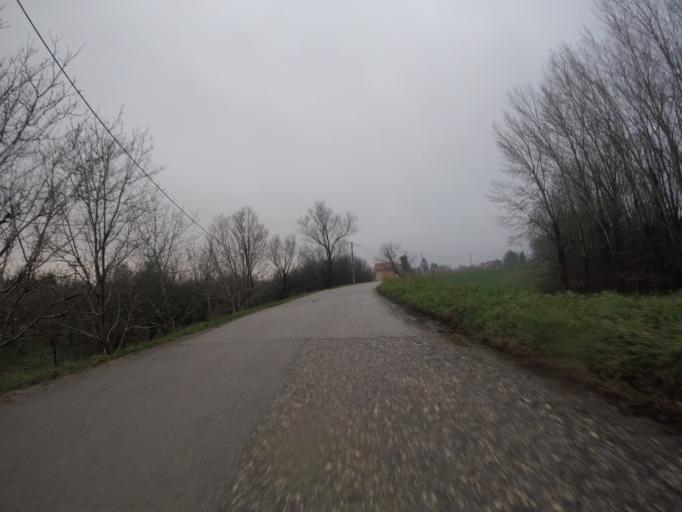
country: HR
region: Zagrebacka
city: Kuce
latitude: 45.7042
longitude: 16.2119
